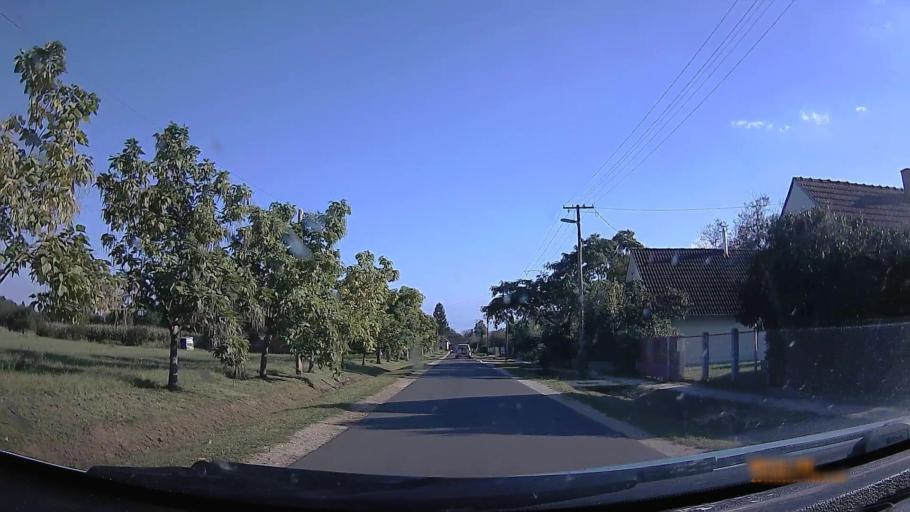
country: HU
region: Zala
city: Pacsa
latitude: 46.6292
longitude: 17.0568
